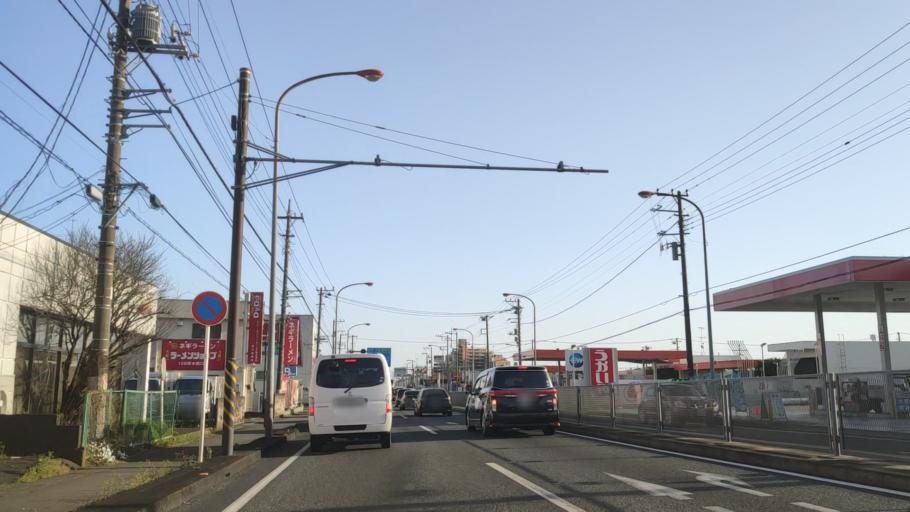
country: JP
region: Kanagawa
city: Zama
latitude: 35.4884
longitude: 139.3647
